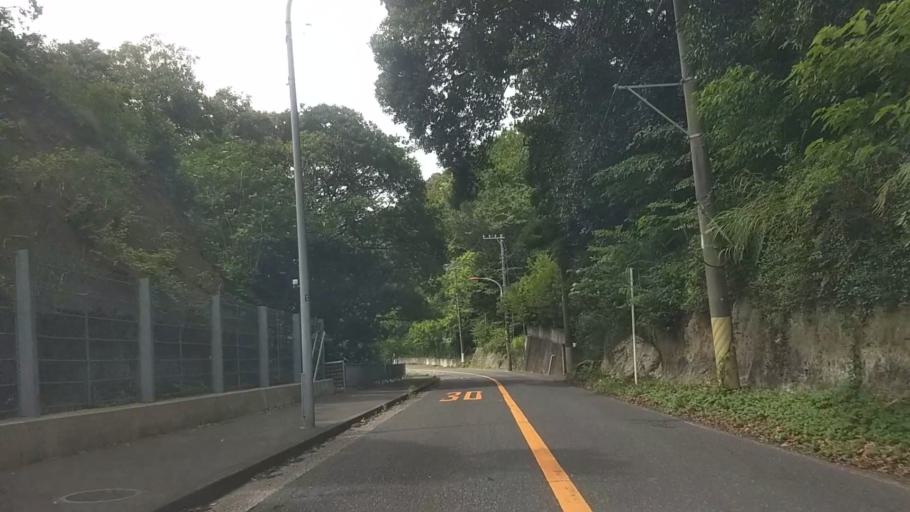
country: JP
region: Kanagawa
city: Yokosuka
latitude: 35.2595
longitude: 139.7173
